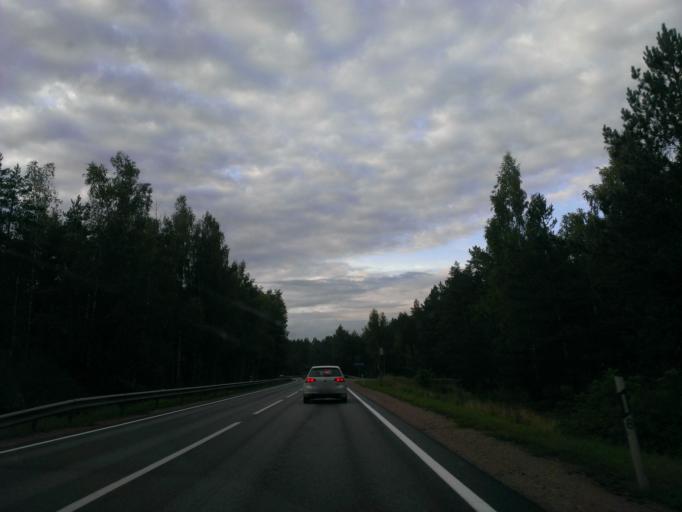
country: LV
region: Riga
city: Bergi
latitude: 56.9561
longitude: 24.3773
